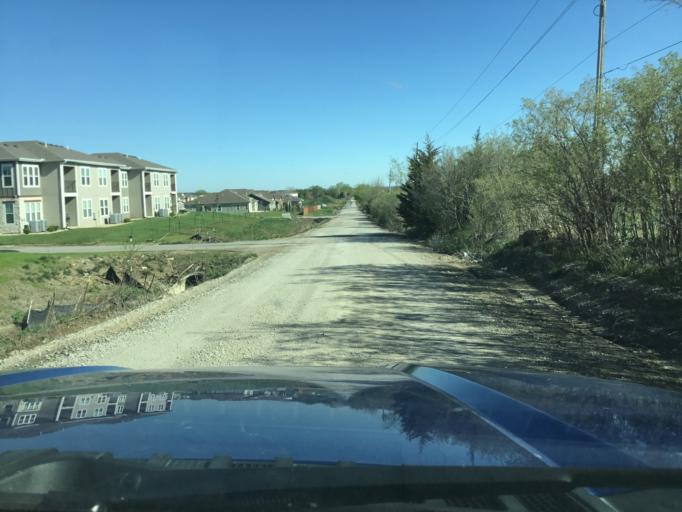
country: US
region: Kansas
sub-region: Douglas County
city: Lawrence
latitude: 38.9760
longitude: -95.3164
